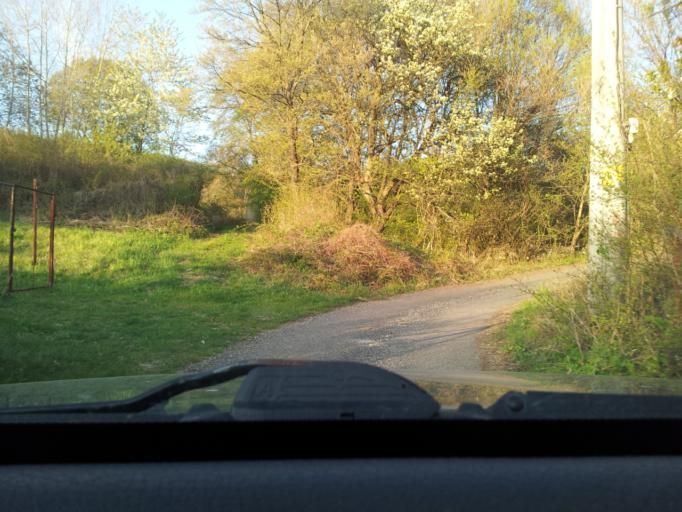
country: SK
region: Nitriansky
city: Tlmace
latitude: 48.3052
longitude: 18.5669
